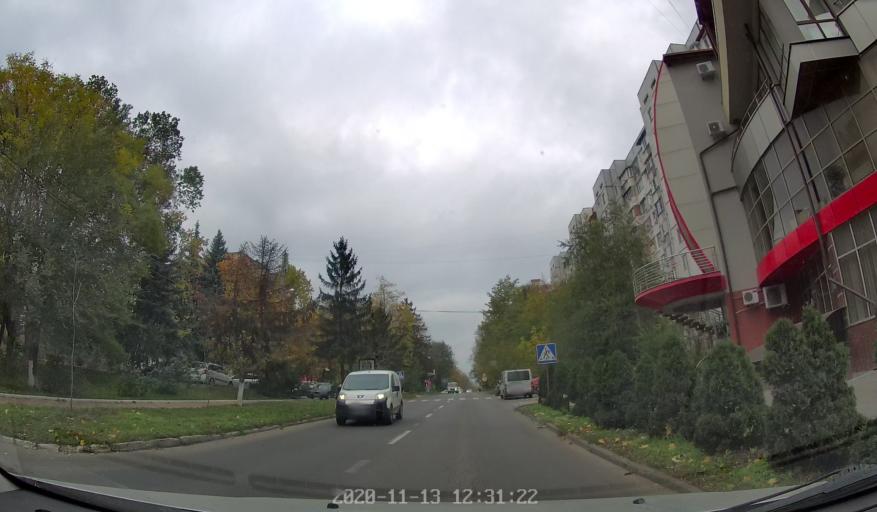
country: MD
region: Chisinau
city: Chisinau
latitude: 46.9784
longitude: 28.8370
